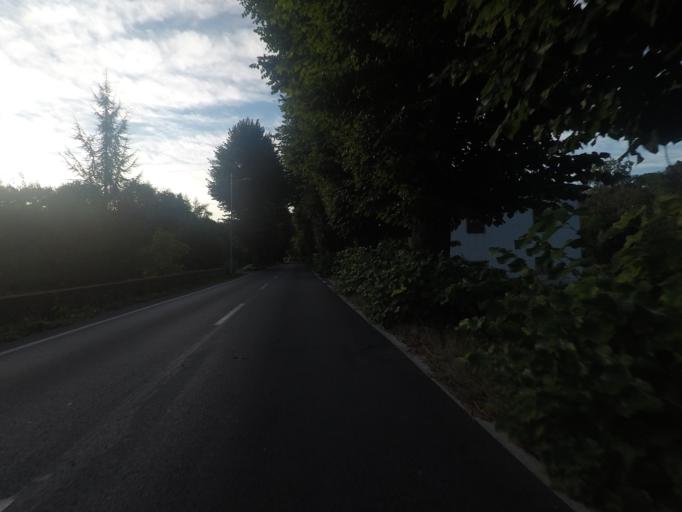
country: IT
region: Tuscany
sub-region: Provincia di Lucca
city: Corsanico-Bargecchia
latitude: 43.9227
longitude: 10.3277
